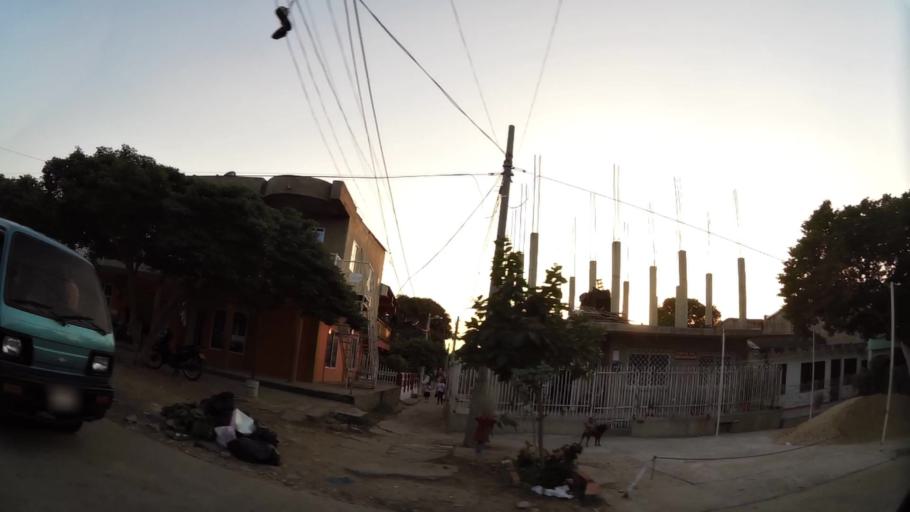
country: CO
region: Bolivar
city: Cartagena
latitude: 10.3862
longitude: -75.4920
